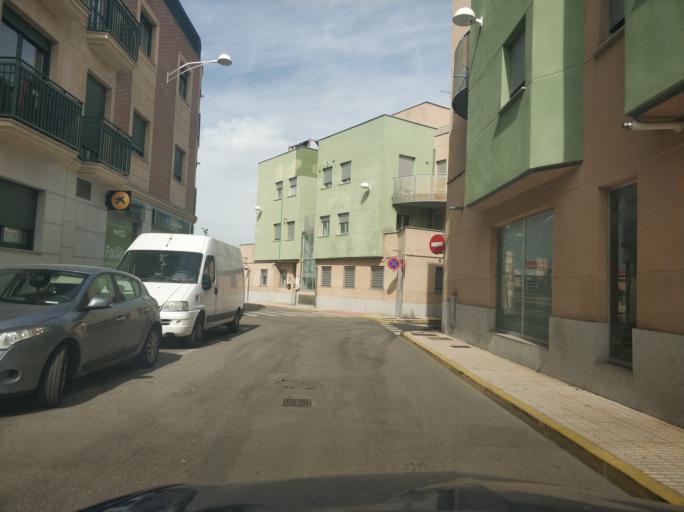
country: ES
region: Castille and Leon
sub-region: Provincia de Salamanca
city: Castellanos de Moriscos
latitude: 41.0188
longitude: -5.5935
